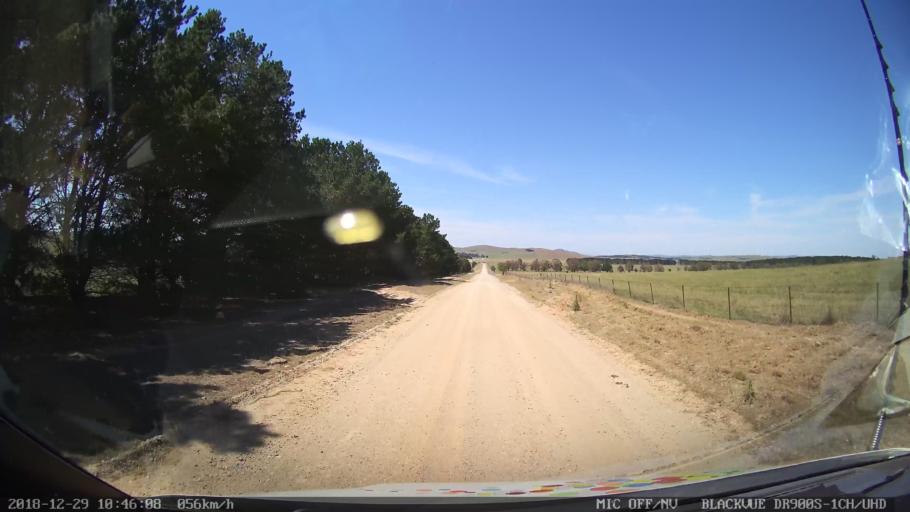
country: AU
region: New South Wales
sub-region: Palerang
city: Bungendore
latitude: -35.0476
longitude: 149.5168
